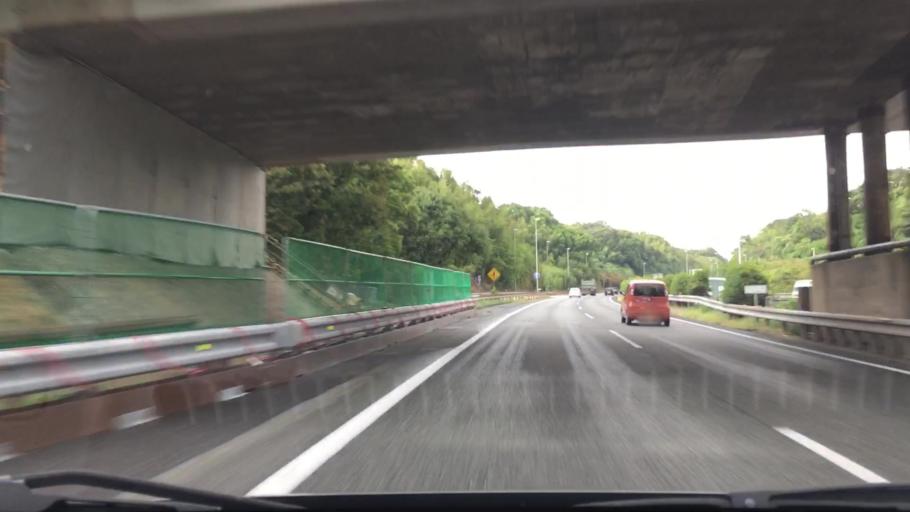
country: JP
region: Fukuoka
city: Koga
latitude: 33.7186
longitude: 130.4931
